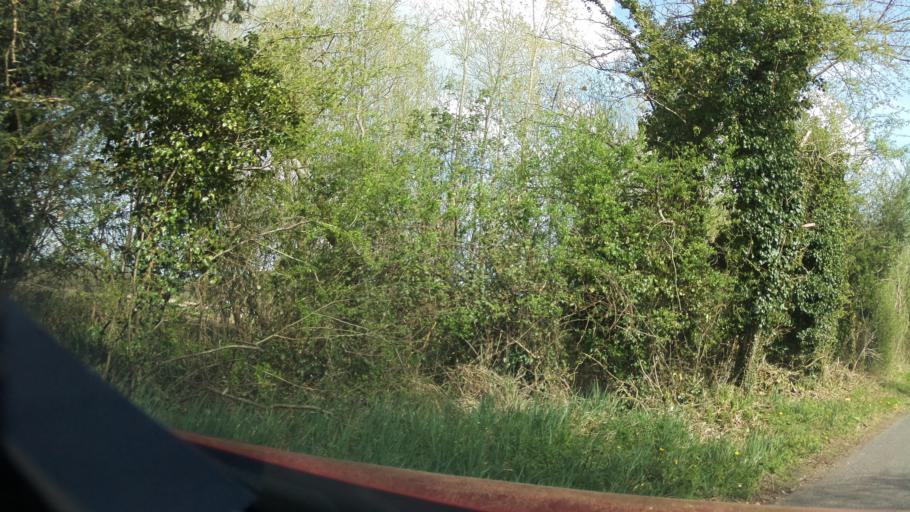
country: GB
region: England
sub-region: Hampshire
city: Romsey
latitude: 51.0745
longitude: -1.5128
